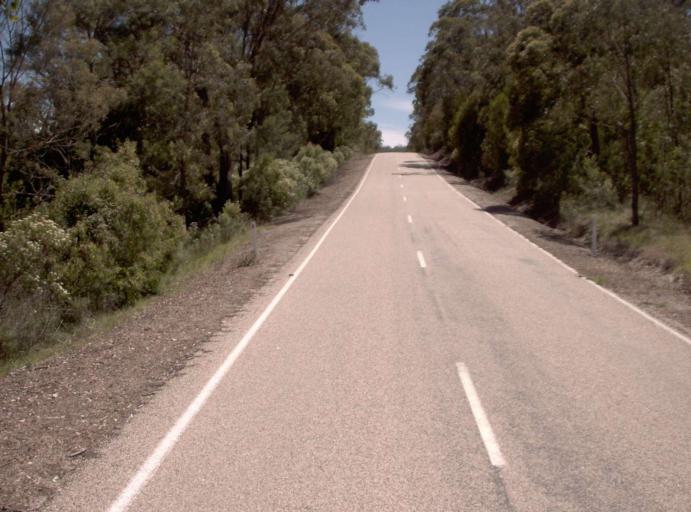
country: AU
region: Victoria
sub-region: East Gippsland
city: Lakes Entrance
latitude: -37.3311
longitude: 148.2340
